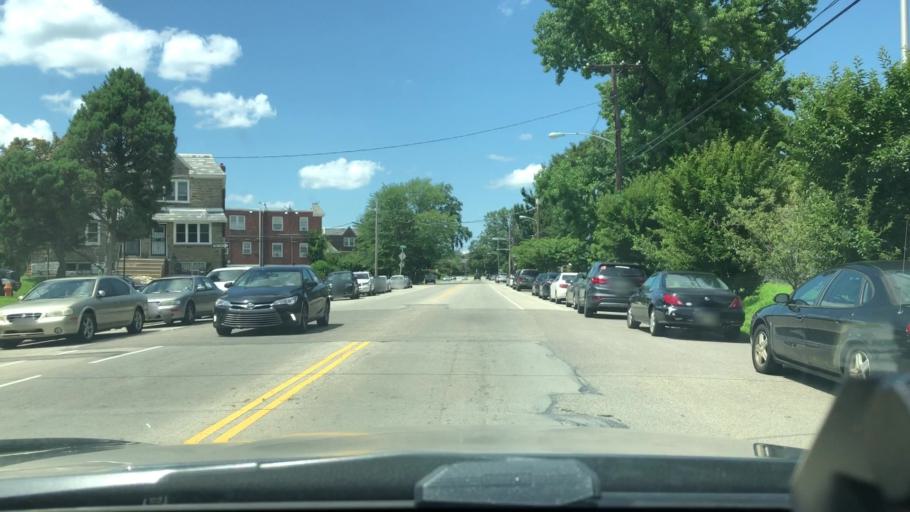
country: US
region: Pennsylvania
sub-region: Montgomery County
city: Wyndmoor
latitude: 40.0637
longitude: -75.1700
